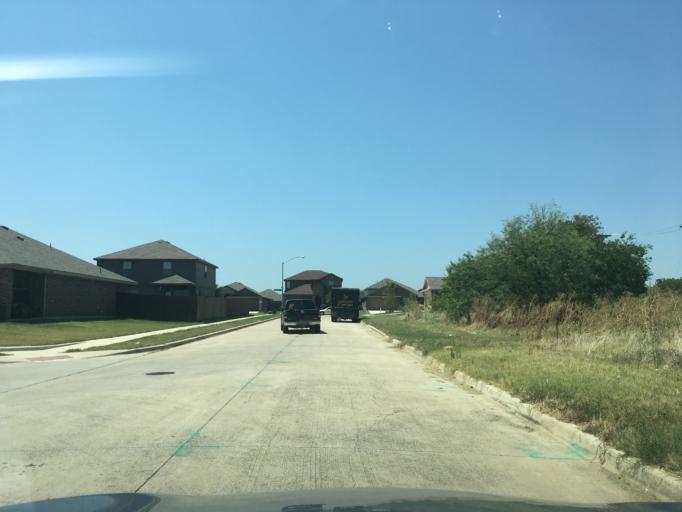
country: US
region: Texas
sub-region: Tarrant County
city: Crowley
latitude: 32.6143
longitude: -97.3622
